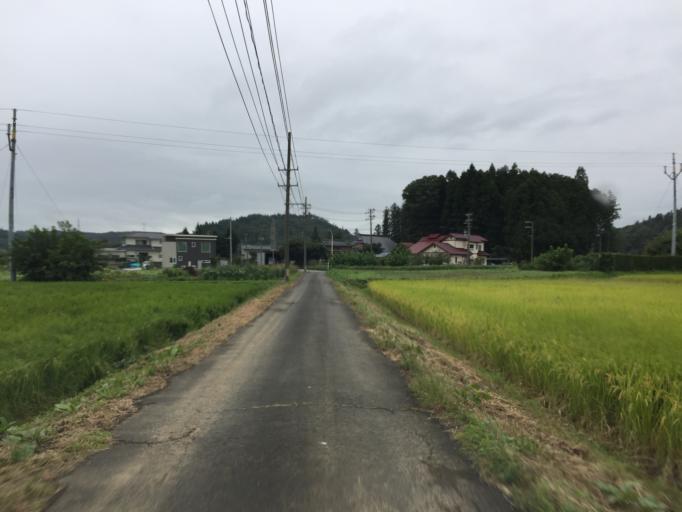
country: JP
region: Fukushima
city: Nihommatsu
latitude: 37.6536
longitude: 140.4464
